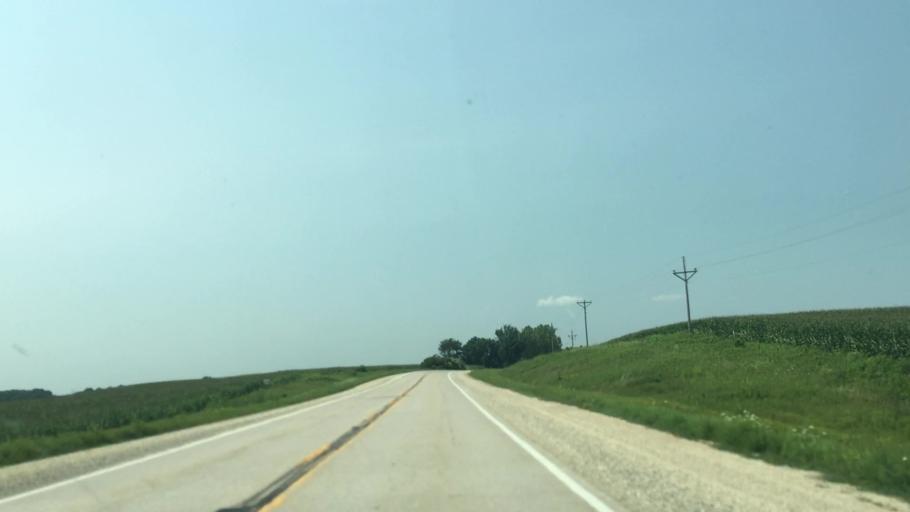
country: US
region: Iowa
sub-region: Fayette County
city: West Union
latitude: 43.0977
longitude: -91.8656
